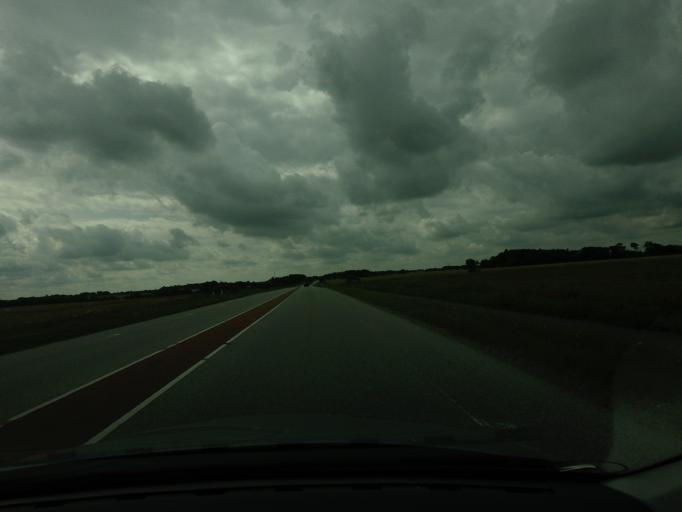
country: DK
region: North Denmark
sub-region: Hjorring Kommune
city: Hjorring
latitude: 57.4136
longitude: 9.9899
